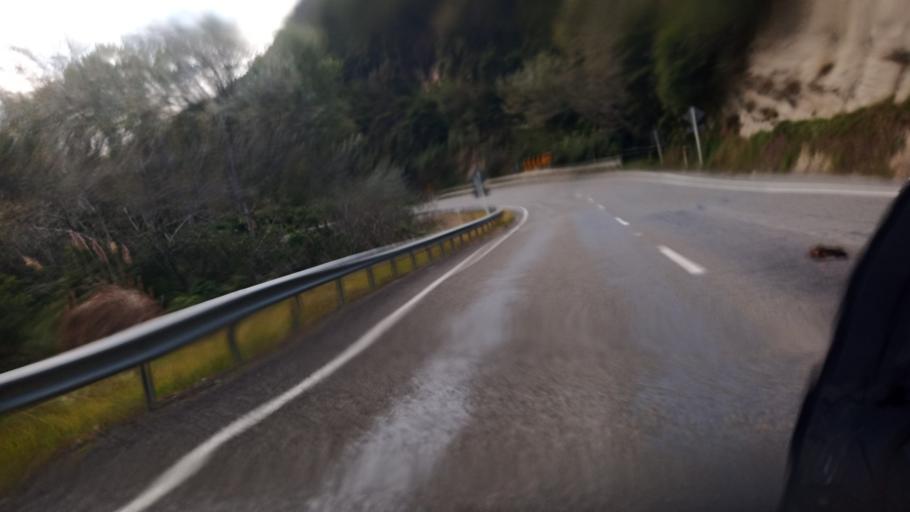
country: NZ
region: Gisborne
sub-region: Gisborne District
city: Gisborne
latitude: -38.4276
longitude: 178.2769
